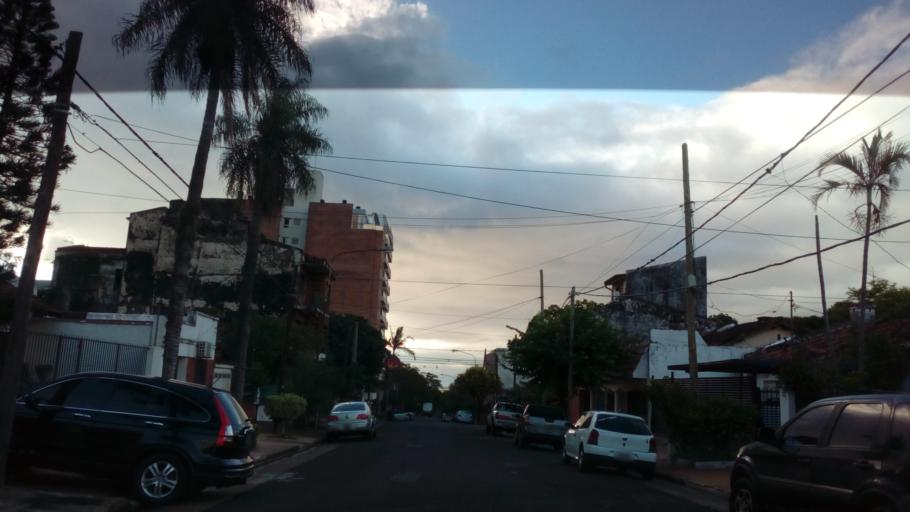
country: AR
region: Misiones
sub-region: Departamento de Capital
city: Posadas
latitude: -27.3541
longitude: -55.8965
